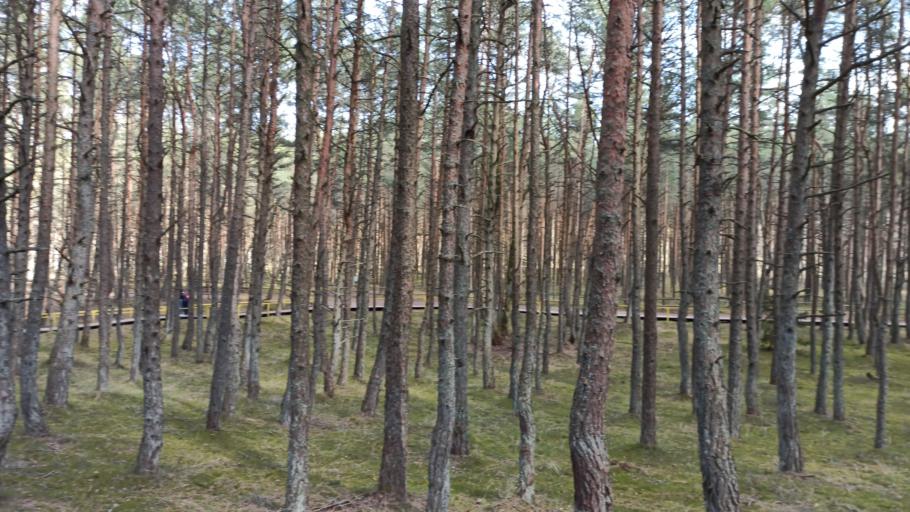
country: LT
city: Nida
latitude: 55.1799
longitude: 20.8624
